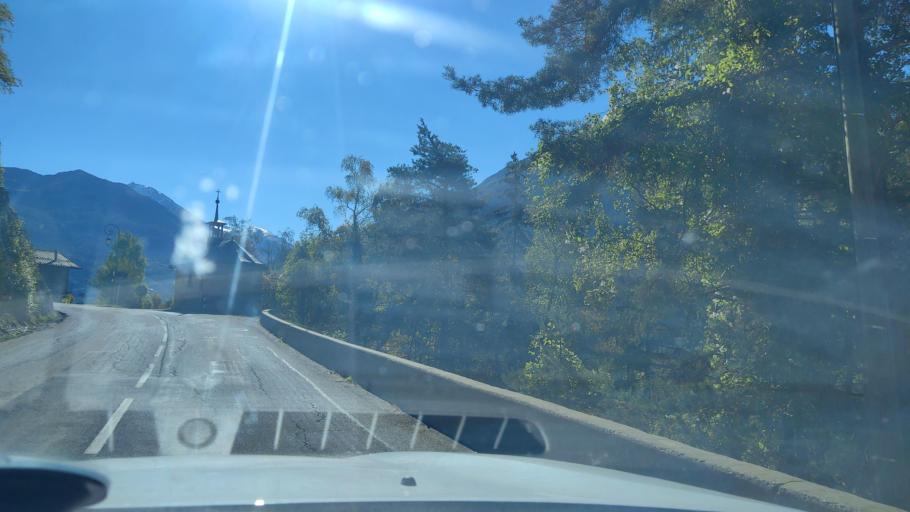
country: FR
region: Rhone-Alpes
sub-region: Departement de la Savoie
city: Seez
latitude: 45.6144
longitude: 6.8371
